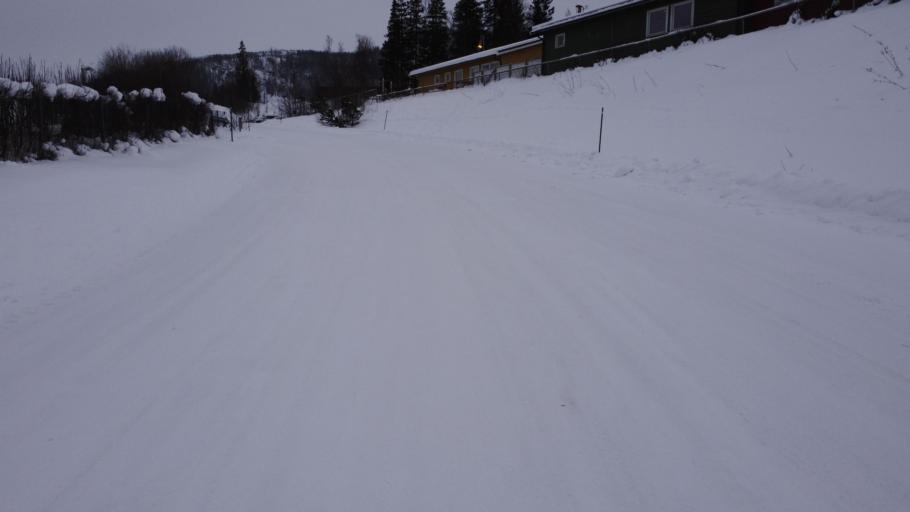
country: NO
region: Nordland
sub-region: Rana
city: Mo i Rana
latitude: 66.3286
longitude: 14.1541
